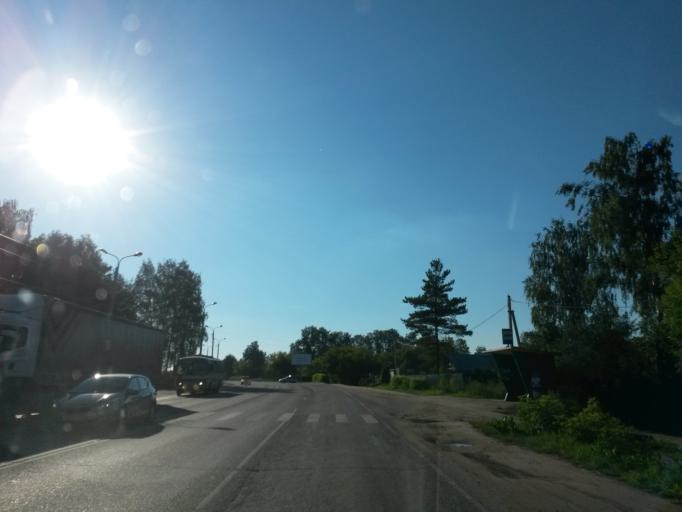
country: RU
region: Ivanovo
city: Novo-Talitsy
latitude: 57.0078
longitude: 40.8645
